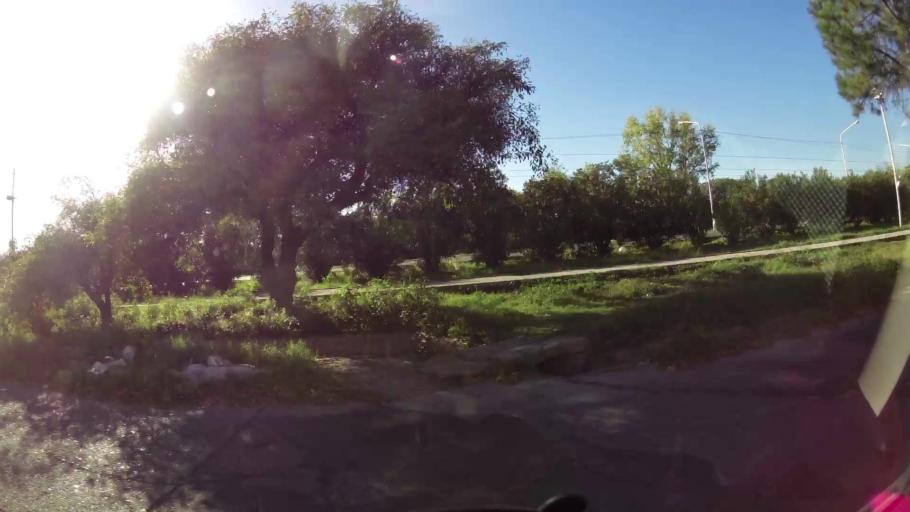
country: AR
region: Mendoza
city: Las Heras
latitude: -32.8642
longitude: -68.8110
